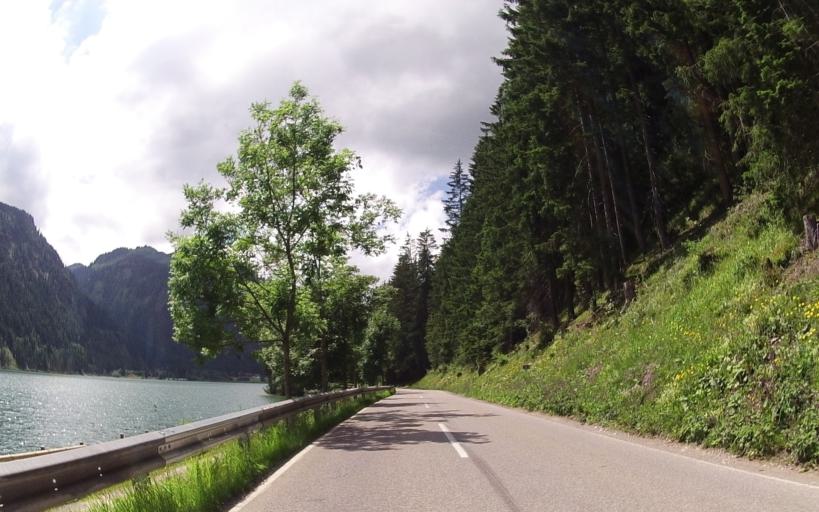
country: AT
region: Tyrol
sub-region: Politischer Bezirk Reutte
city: Graen
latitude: 47.4950
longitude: 10.5817
